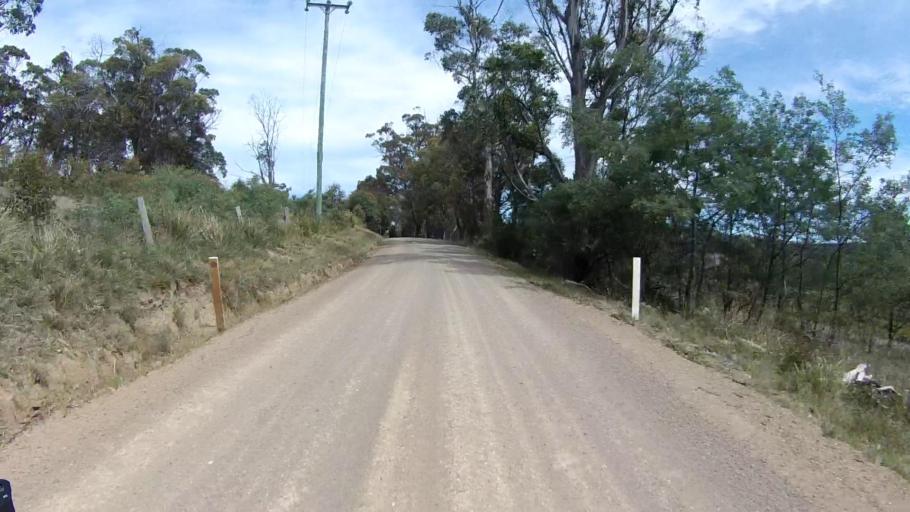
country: AU
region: Tasmania
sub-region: Sorell
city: Sorell
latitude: -42.7929
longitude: 147.6921
